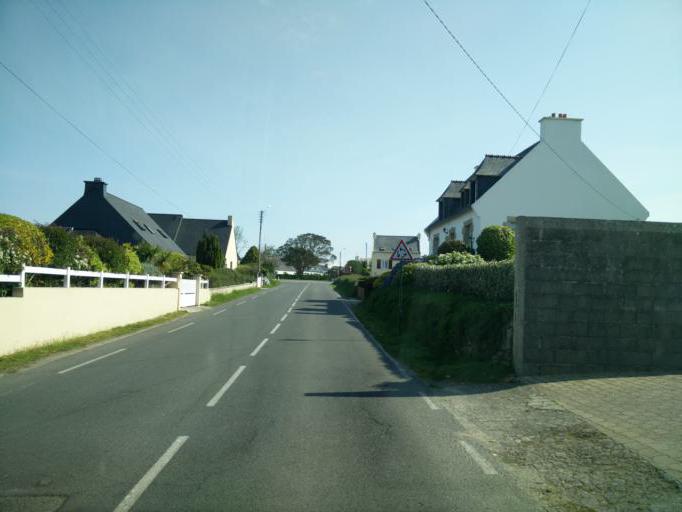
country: FR
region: Brittany
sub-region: Departement du Finistere
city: Crozon
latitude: 48.2437
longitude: -4.4837
